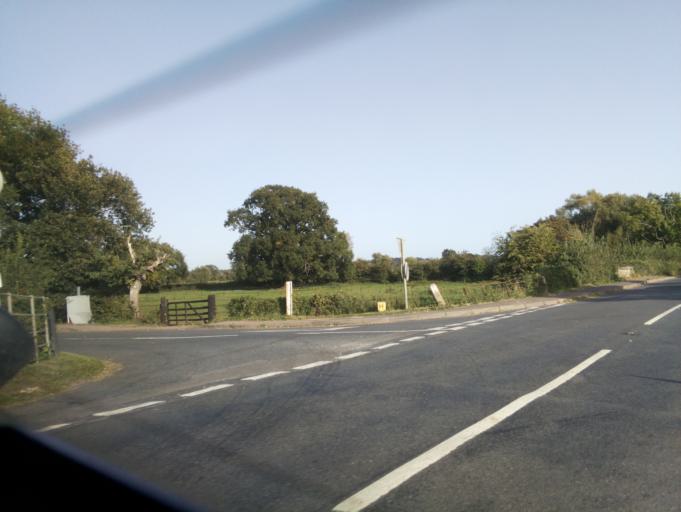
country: GB
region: England
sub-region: Gloucestershire
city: Tewkesbury
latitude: 51.9534
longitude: -2.2361
